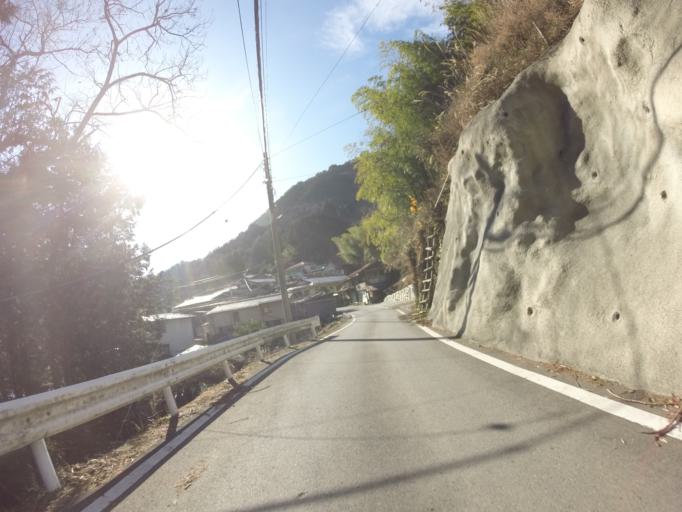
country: JP
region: Yamanashi
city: Ryuo
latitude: 35.3980
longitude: 138.3238
